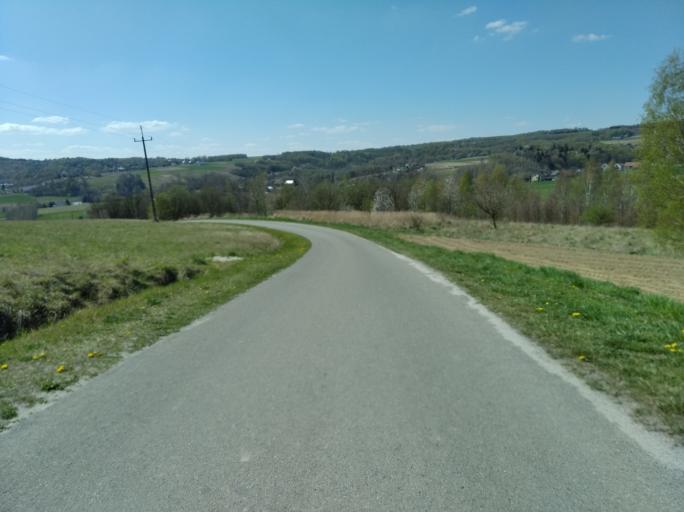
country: PL
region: Subcarpathian Voivodeship
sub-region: Powiat strzyzowski
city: Wisniowa
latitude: 49.9172
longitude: 21.6759
